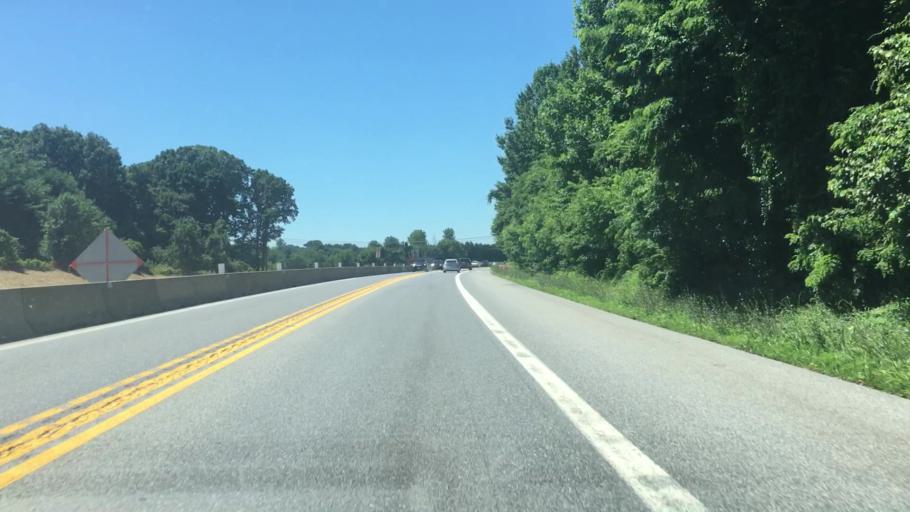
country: US
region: Maryland
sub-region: Howard County
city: Highland
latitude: 39.2193
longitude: -76.9659
